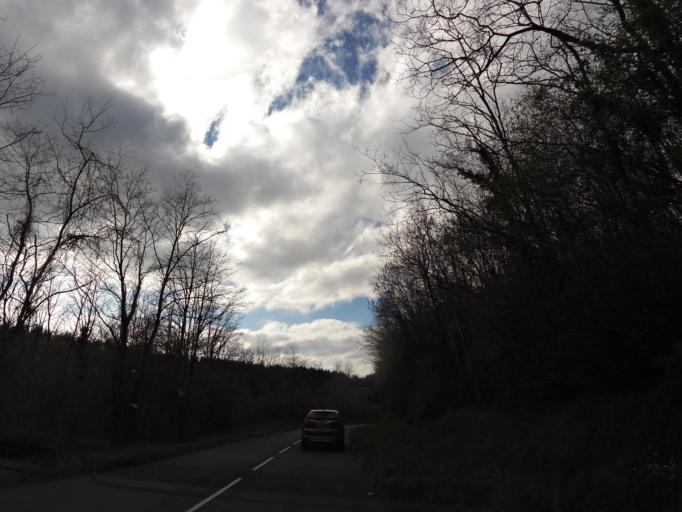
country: FR
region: Midi-Pyrenees
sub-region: Departement du Tarn
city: Soreze
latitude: 43.4141
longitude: 2.0635
